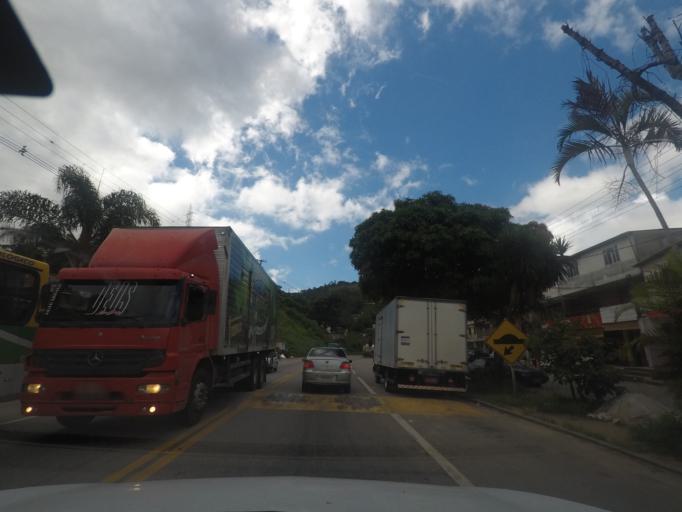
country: BR
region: Rio de Janeiro
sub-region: Teresopolis
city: Teresopolis
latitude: -22.3938
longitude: -42.9528
